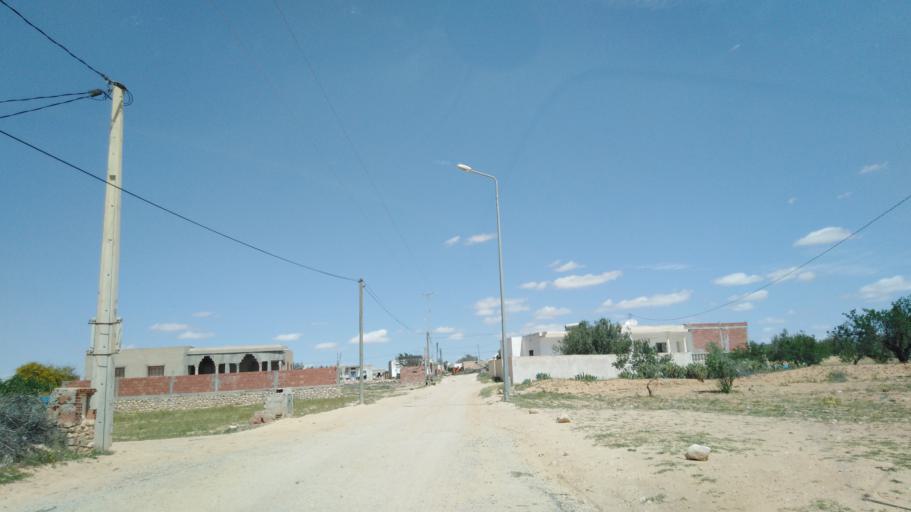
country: TN
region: Safaqis
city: Sfax
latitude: 34.7454
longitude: 10.5514
